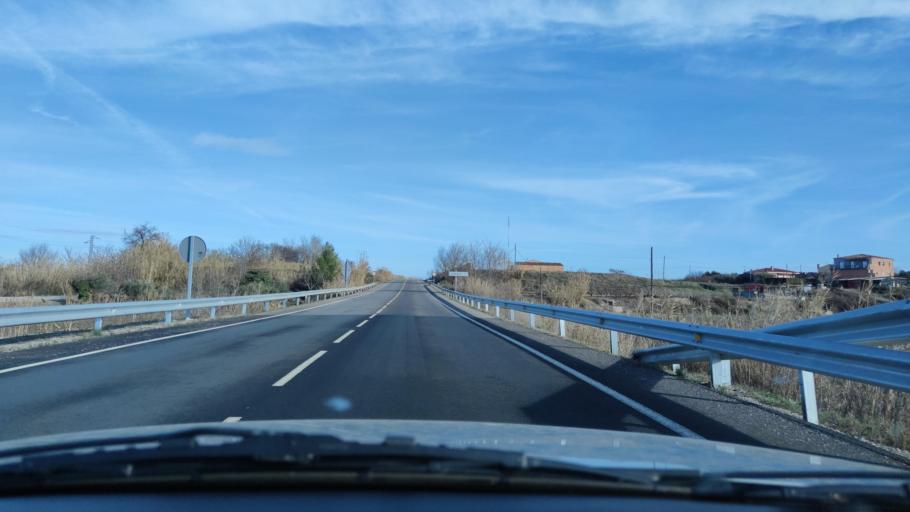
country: ES
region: Catalonia
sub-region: Provincia de Lleida
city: Lleida
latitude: 41.5890
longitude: 0.6308
